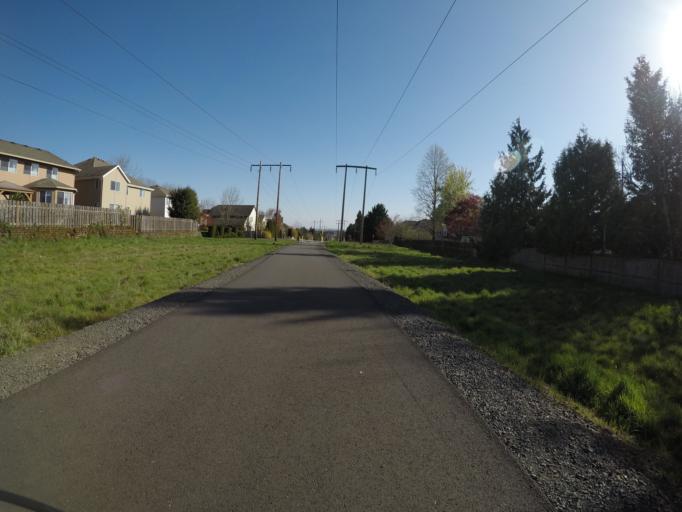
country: US
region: Oregon
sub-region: Washington County
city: Oak Hills
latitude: 45.5577
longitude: -122.8261
